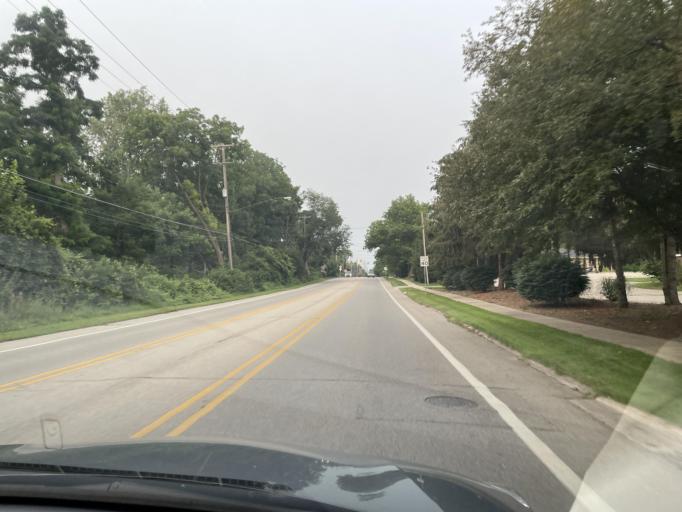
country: US
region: Michigan
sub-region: Kent County
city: East Grand Rapids
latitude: 42.9627
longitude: -85.6248
